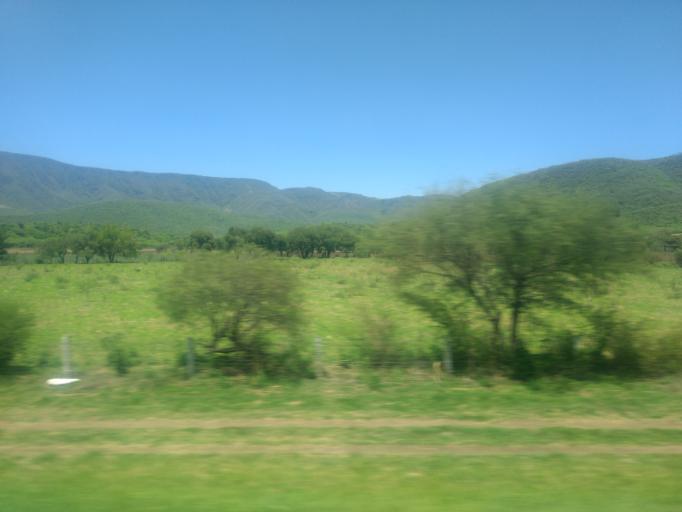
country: MX
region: Jalisco
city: Zacoalco de Torres
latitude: 20.2176
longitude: -103.5308
